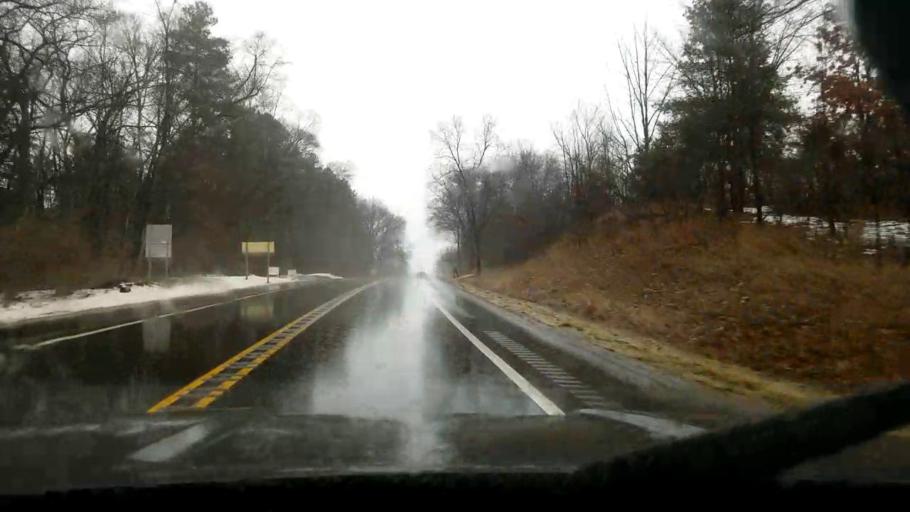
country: US
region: Michigan
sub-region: Jackson County
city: Napoleon
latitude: 42.1826
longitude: -84.2955
